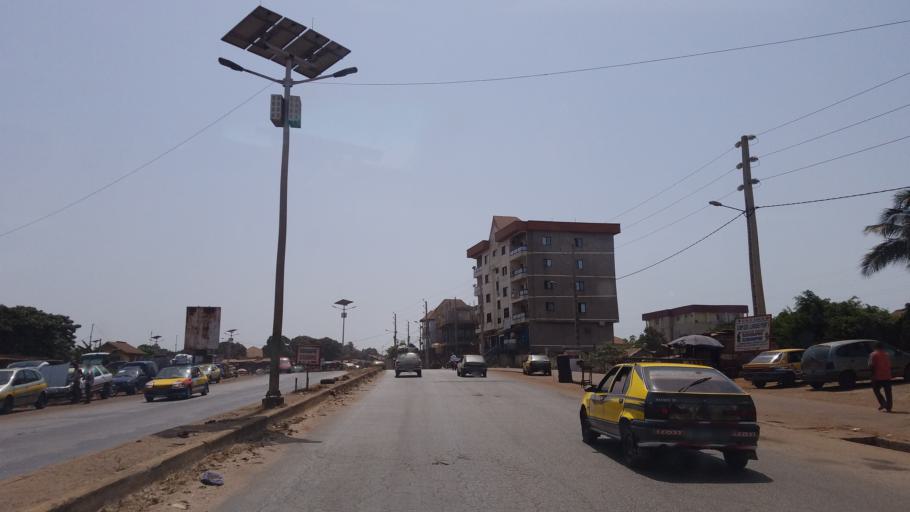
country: GN
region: Conakry
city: Conakry
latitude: 9.6491
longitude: -13.5842
